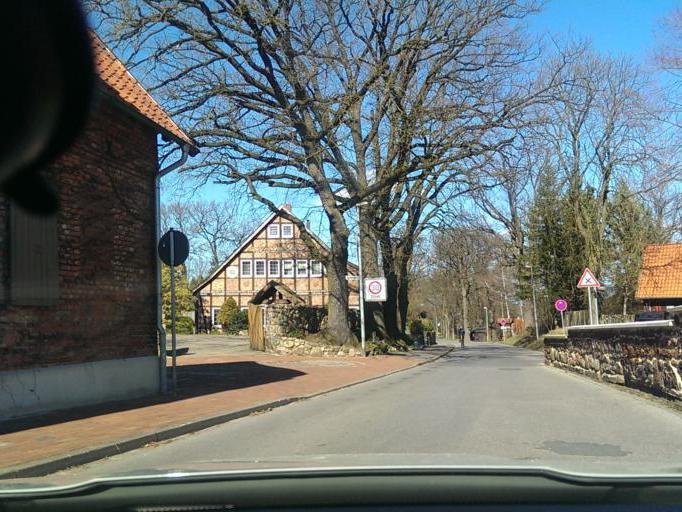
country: DE
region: Lower Saxony
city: Elze
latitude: 52.5240
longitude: 9.7567
